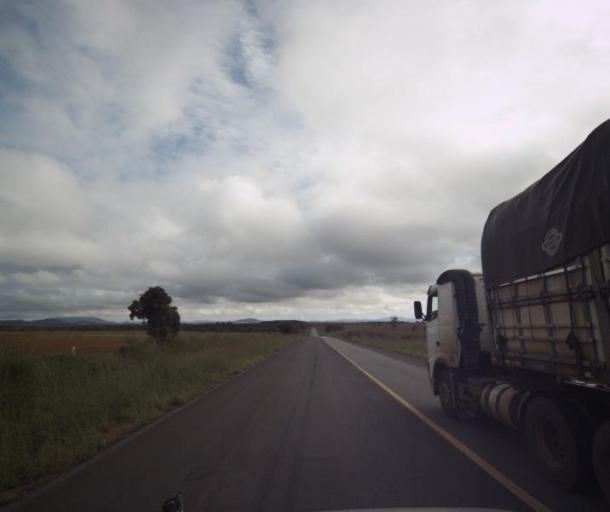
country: BR
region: Goias
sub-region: Padre Bernardo
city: Padre Bernardo
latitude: -15.3485
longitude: -48.6471
